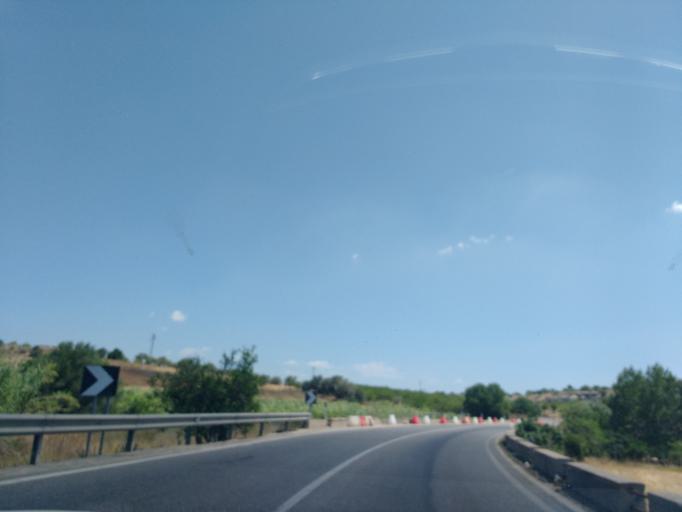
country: IT
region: Sicily
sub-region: Provincia di Siracusa
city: Rosolini
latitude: 36.8404
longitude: 14.9829
